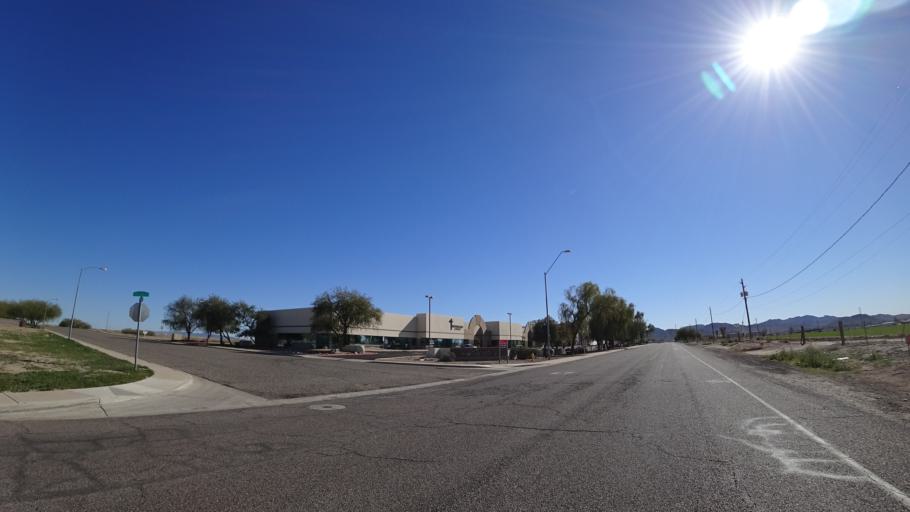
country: US
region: Arizona
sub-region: Maricopa County
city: Goodyear
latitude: 33.4139
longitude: -112.3752
